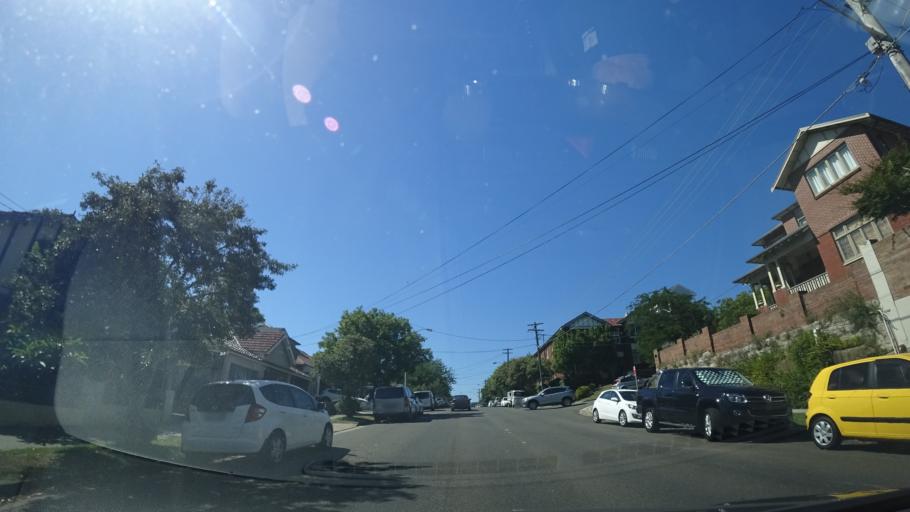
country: AU
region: New South Wales
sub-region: Randwick
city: Randwick
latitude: -33.9068
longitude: 151.2469
